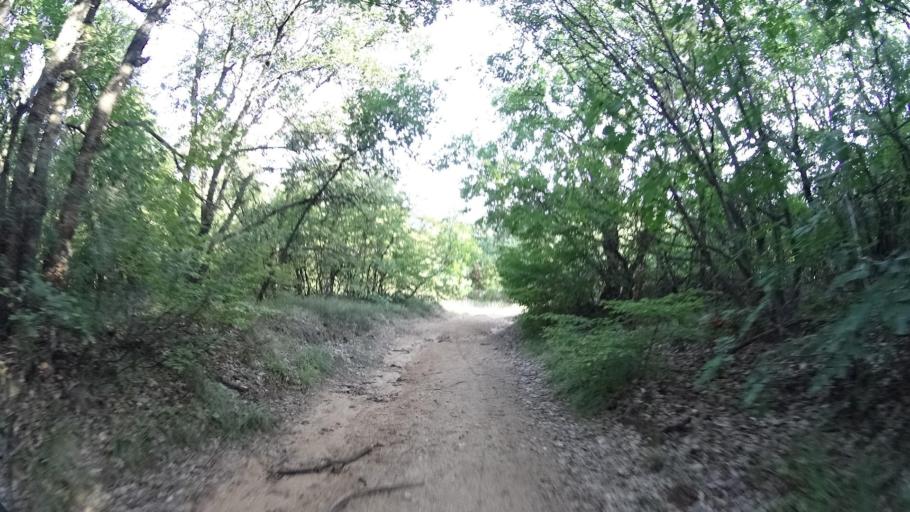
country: BG
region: Plovdiv
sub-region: Obshtina Plovdiv
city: Plovdiv
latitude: 42.0538
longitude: 24.6876
